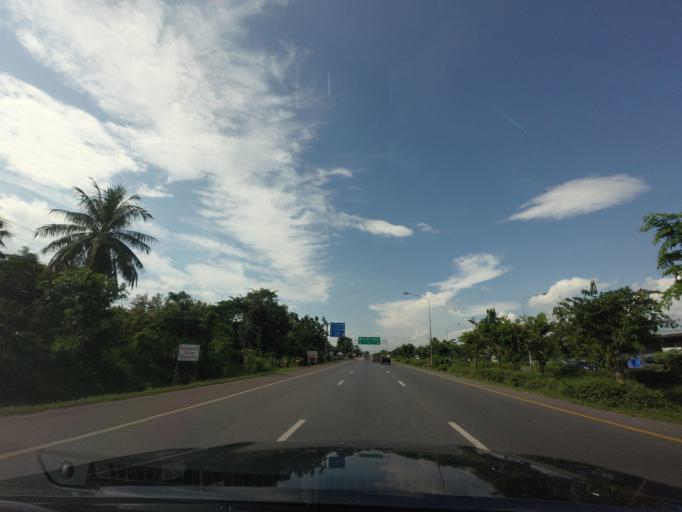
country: TH
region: Nong Khai
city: Sa Khrai
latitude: 17.6832
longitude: 102.7842
